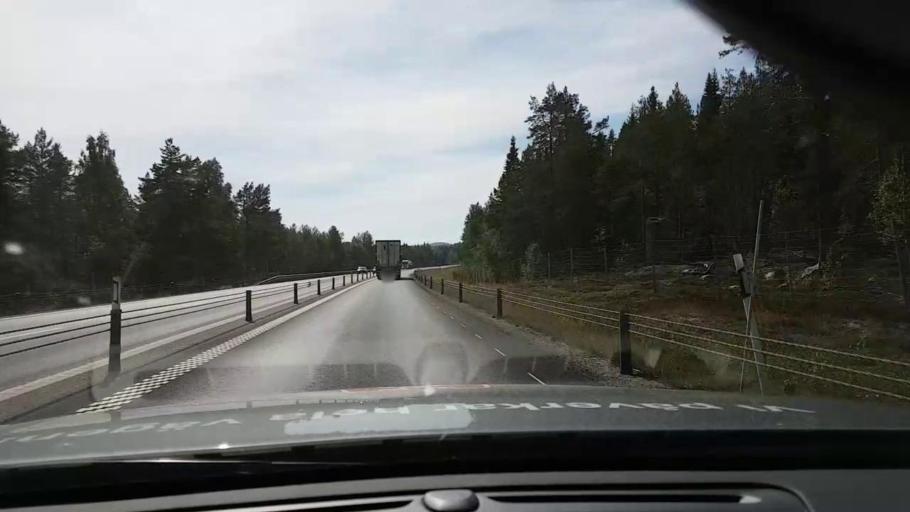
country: SE
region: Vaesternorrland
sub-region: OErnskoeldsviks Kommun
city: Husum
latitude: 63.4742
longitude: 19.2869
